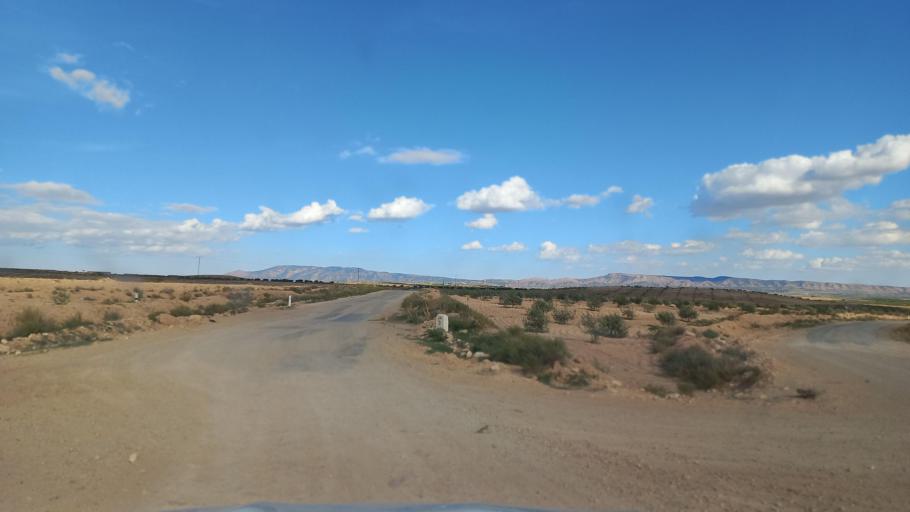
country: TN
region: Al Qasrayn
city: Sbiba
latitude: 35.3924
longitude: 9.0188
